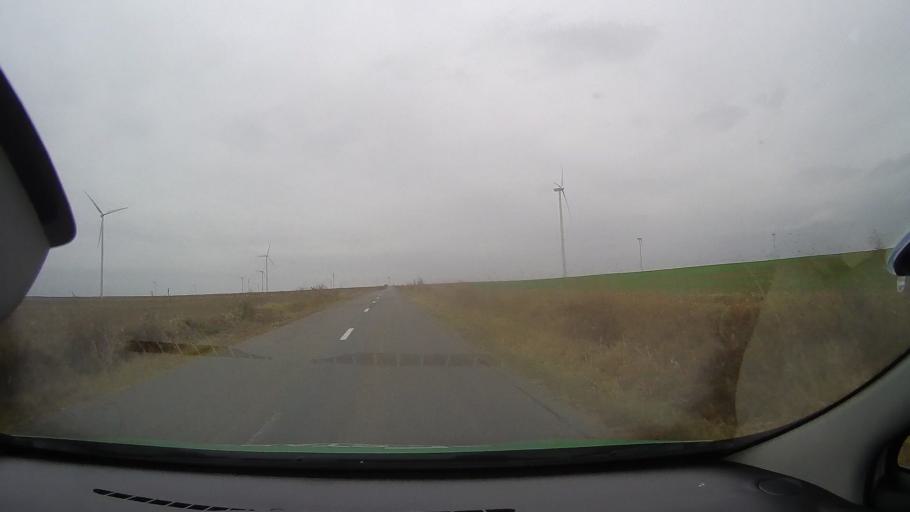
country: RO
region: Constanta
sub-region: Comuna Pantelimon
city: Pantelimon
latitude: 44.5042
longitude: 28.3488
